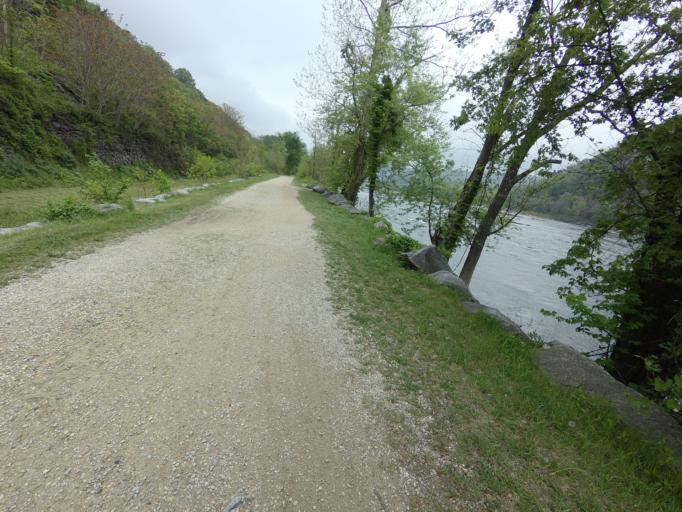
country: US
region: West Virginia
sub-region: Jefferson County
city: Bolivar
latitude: 39.3234
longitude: -77.7239
